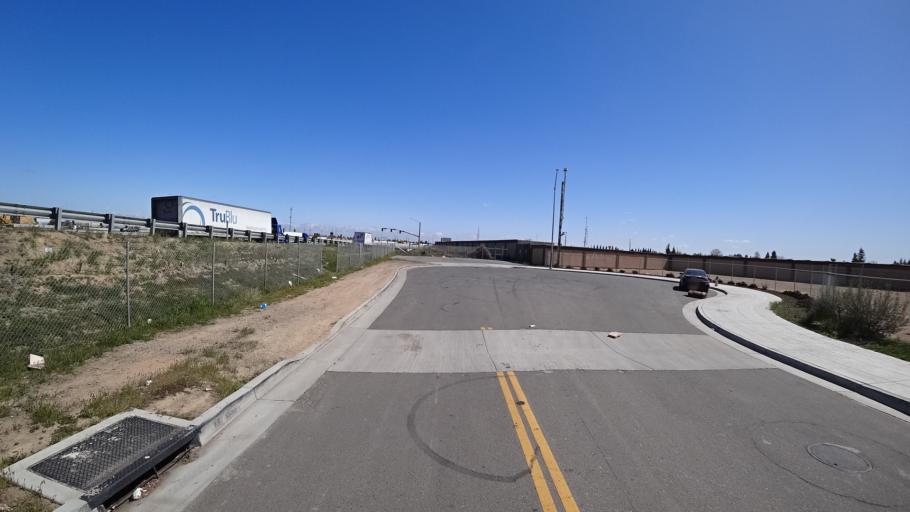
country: US
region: California
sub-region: Fresno County
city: West Park
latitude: 36.7898
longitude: -119.8599
